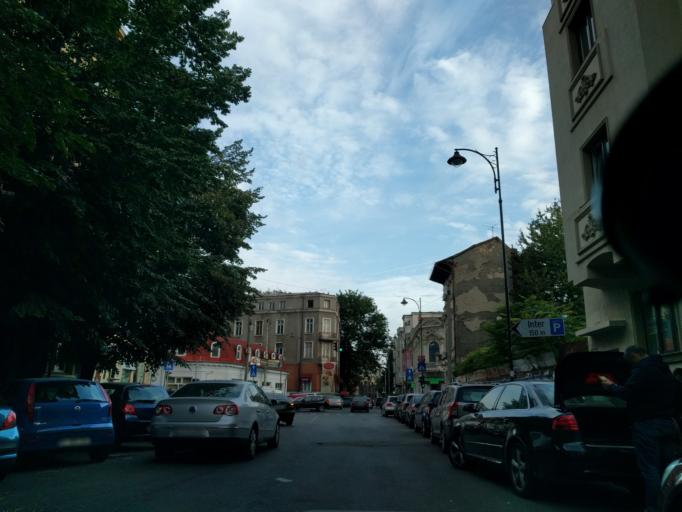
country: RO
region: Bucuresti
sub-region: Municipiul Bucuresti
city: Bucharest
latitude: 44.4386
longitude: 26.1053
